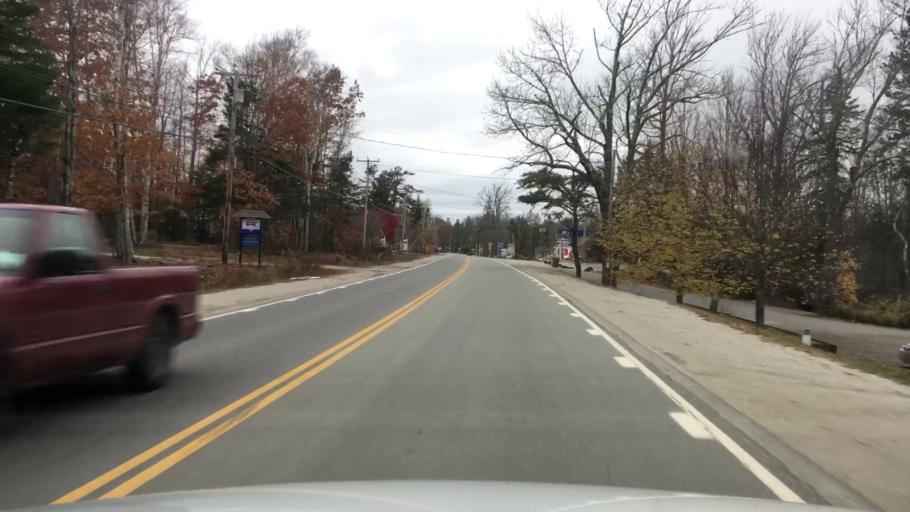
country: US
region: Maine
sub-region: Hancock County
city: Sedgwick
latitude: 44.4054
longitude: -68.5941
